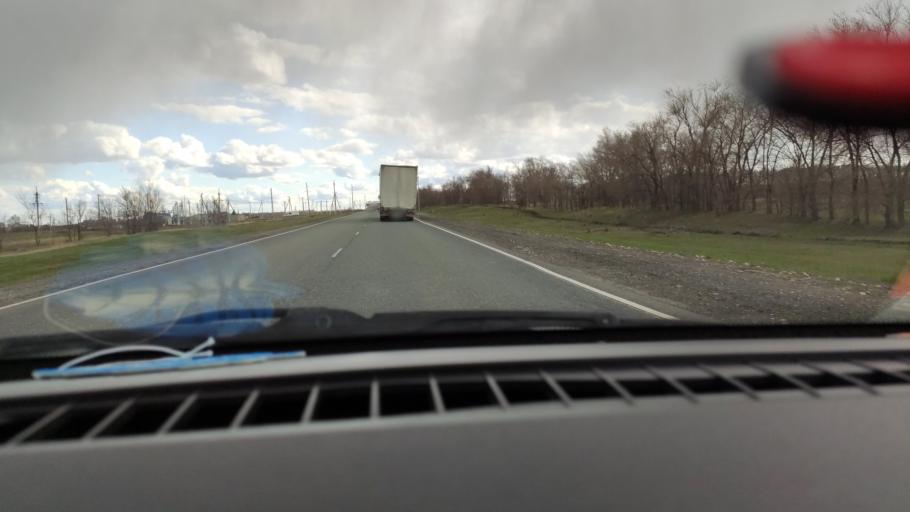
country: RU
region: Saratov
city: Balakovo
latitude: 52.1188
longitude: 47.7519
